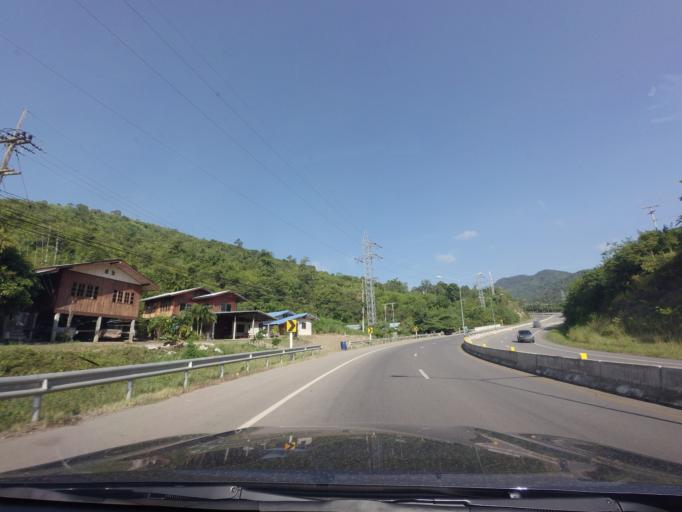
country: TH
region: Phetchabun
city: Lom Sak
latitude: 16.7637
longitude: 101.1409
